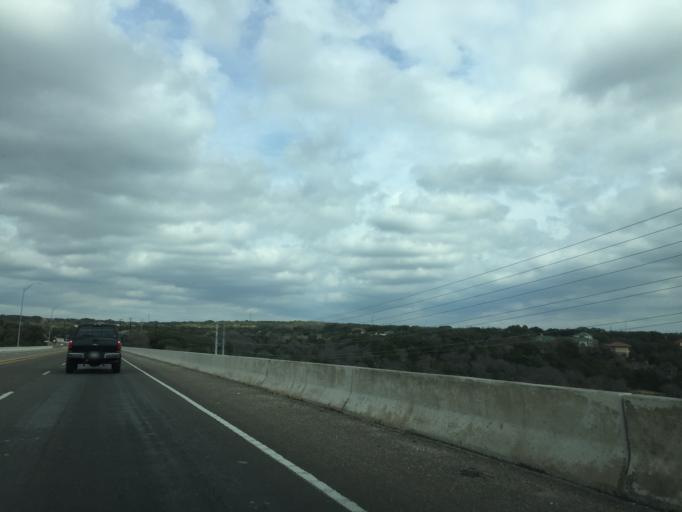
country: US
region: Texas
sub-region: Travis County
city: Briarcliff
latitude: 30.3884
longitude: -98.0863
